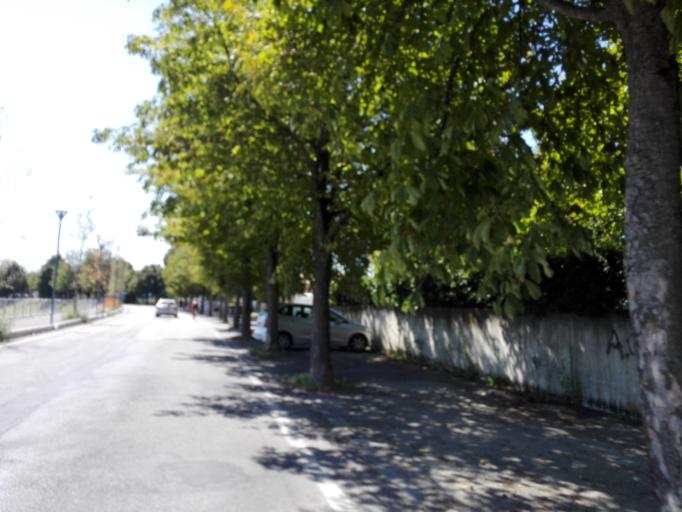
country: IT
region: Umbria
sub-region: Provincia di Perugia
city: Foligno
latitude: 42.9555
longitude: 12.6947
